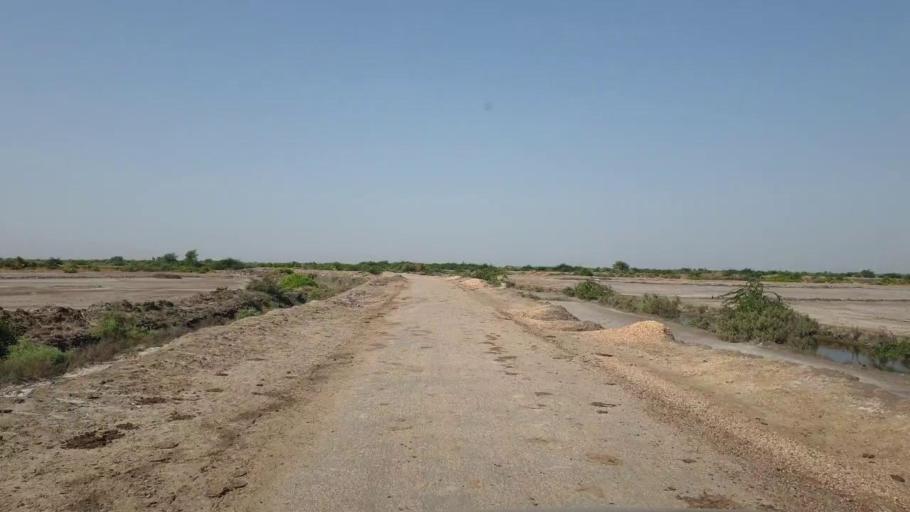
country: PK
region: Sindh
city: Tando Bago
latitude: 24.7085
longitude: 69.0742
